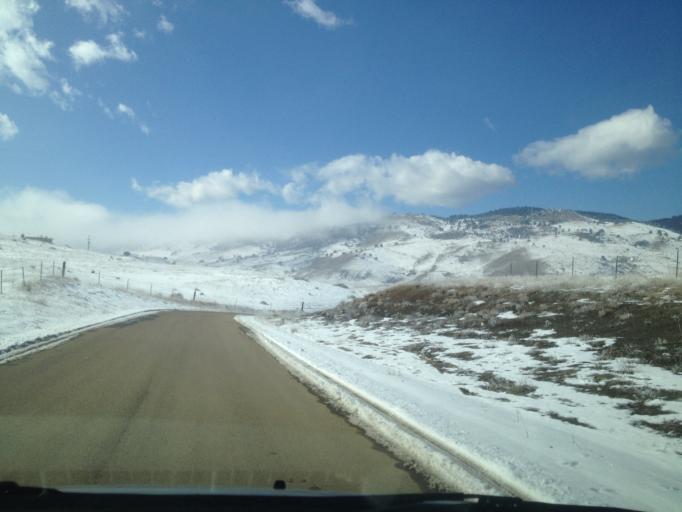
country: US
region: Colorado
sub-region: Boulder County
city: Boulder
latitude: 40.0797
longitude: -105.2744
